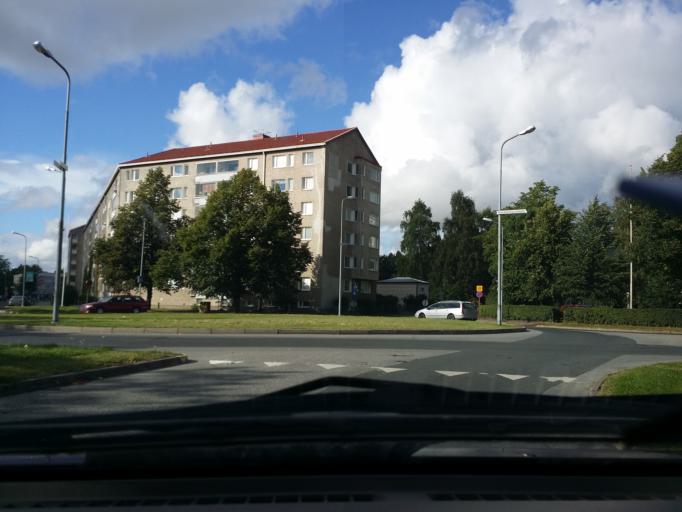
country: FI
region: Satakunta
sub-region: Pori
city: Pori
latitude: 61.4771
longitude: 21.7931
